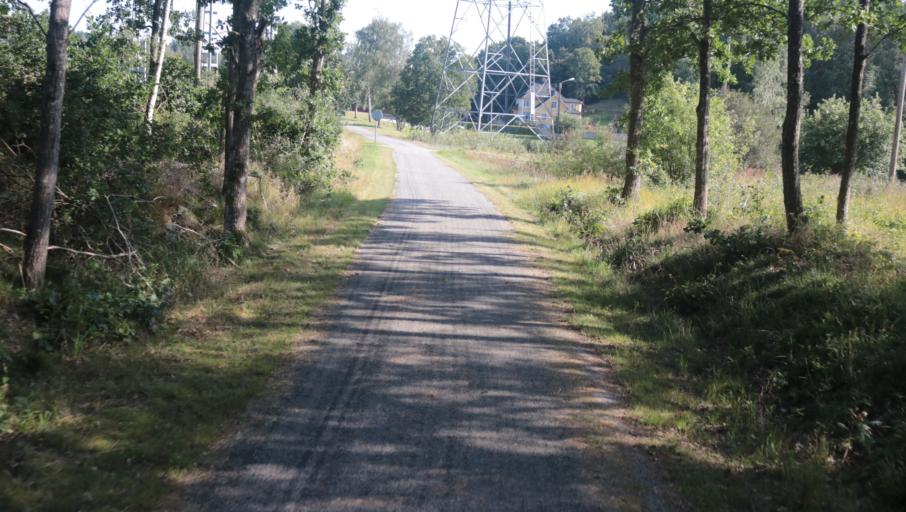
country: SE
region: Blekinge
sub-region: Karlshamns Kommun
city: Svangsta
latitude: 56.3875
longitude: 14.6757
